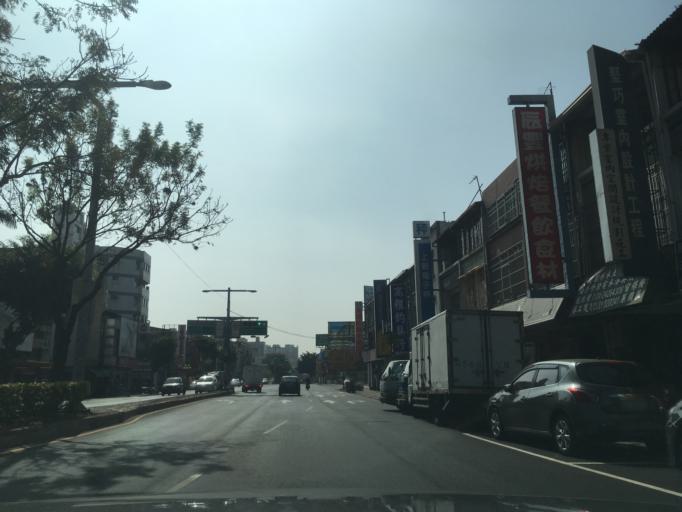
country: TW
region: Taiwan
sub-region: Taichung City
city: Taichung
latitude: 24.1940
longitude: 120.6591
